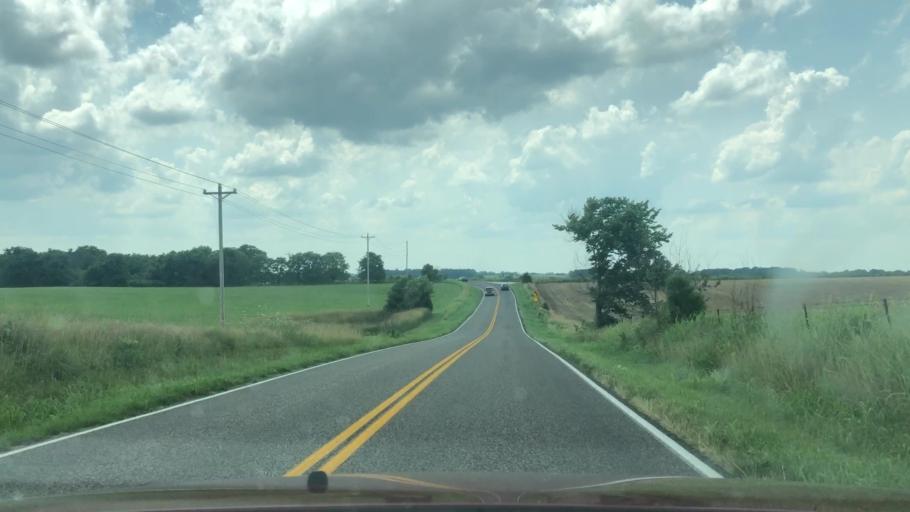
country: US
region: Missouri
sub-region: Christian County
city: Ozark
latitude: 36.9431
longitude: -93.2465
